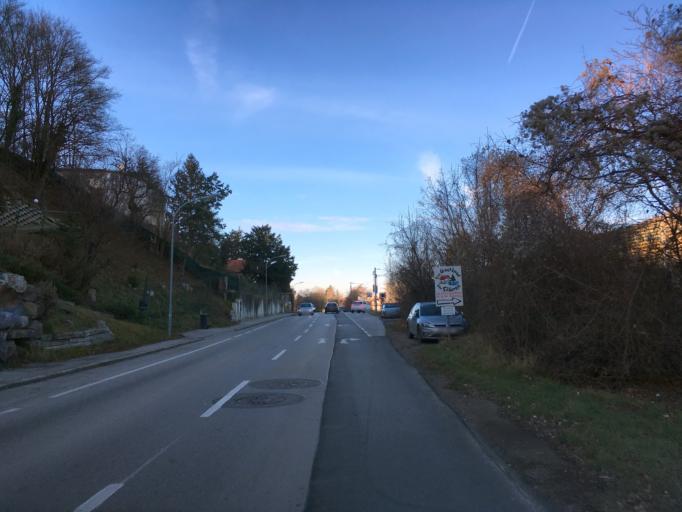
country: AT
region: Lower Austria
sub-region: Politischer Bezirk Korneuburg
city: Korneuburg
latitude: 48.3449
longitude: 16.2904
